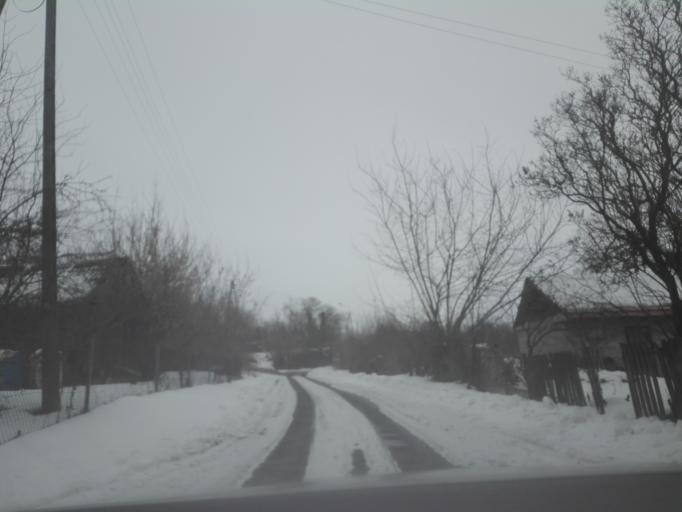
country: PL
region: Lublin Voivodeship
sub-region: Powiat hrubieszowski
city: Horodlo
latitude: 50.8465
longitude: 24.0265
